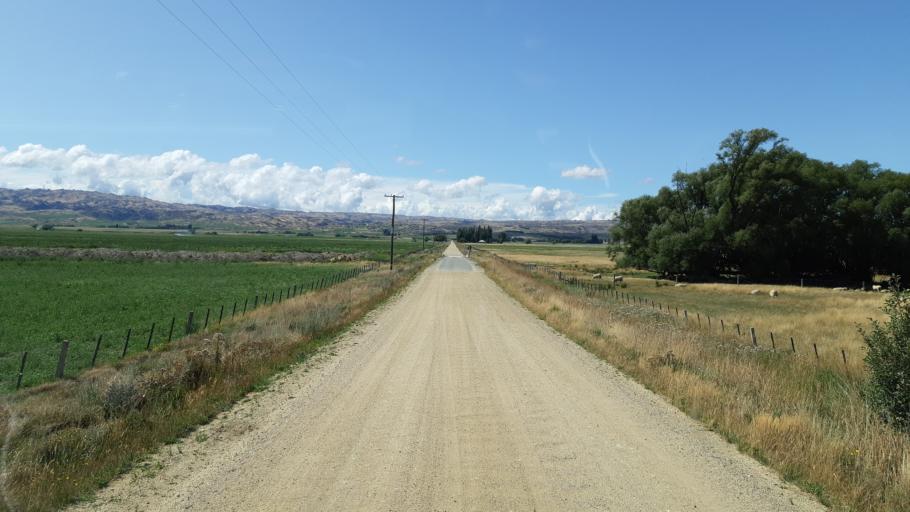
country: NZ
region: Otago
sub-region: Queenstown-Lakes District
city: Wanaka
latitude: -45.2033
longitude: 169.6499
